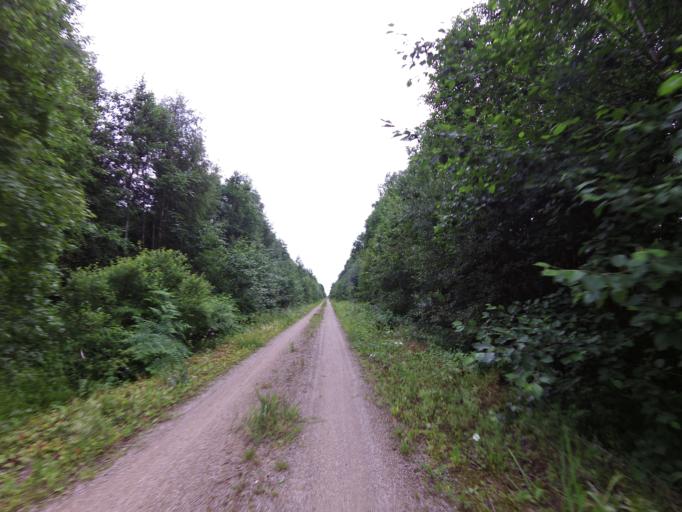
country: EE
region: Harju
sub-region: Nissi vald
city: Turba
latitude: 59.0208
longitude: 24.0996
